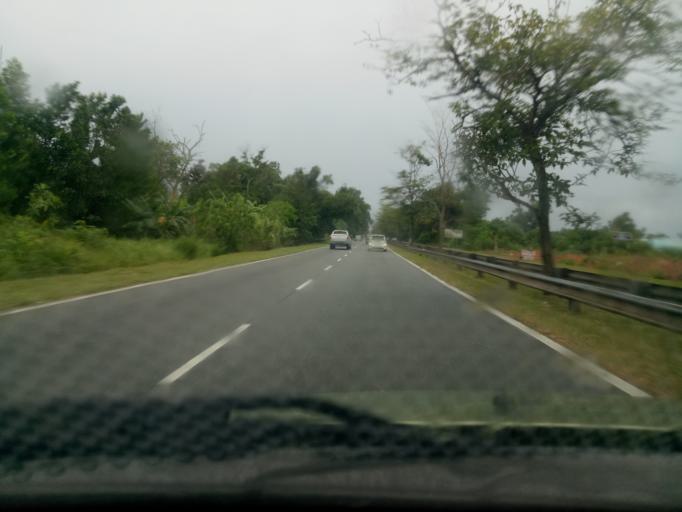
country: MY
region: Kedah
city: Sungai Petani
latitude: 5.6419
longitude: 100.5393
